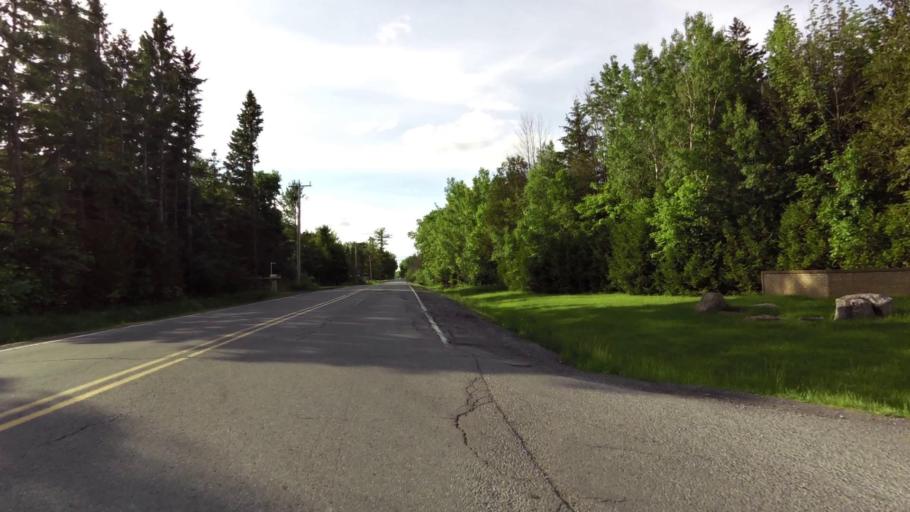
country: CA
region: Ontario
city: Ottawa
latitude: 45.2367
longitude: -75.6124
